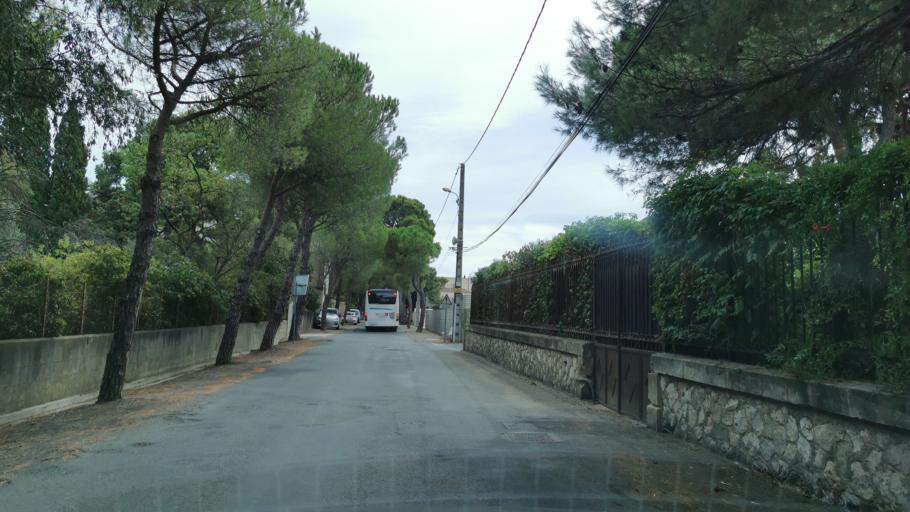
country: FR
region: Languedoc-Roussillon
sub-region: Departement de l'Aude
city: Argeliers
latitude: 43.3087
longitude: 2.9135
